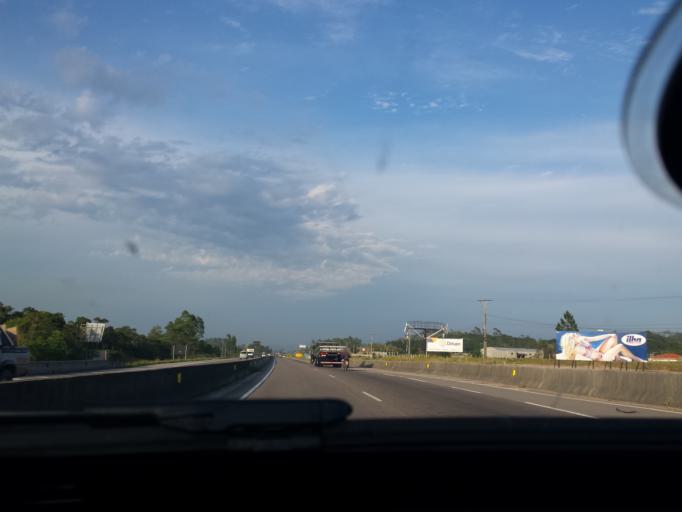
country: BR
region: Santa Catarina
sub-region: Tubarao
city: Tubarao
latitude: -28.4249
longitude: -48.9026
